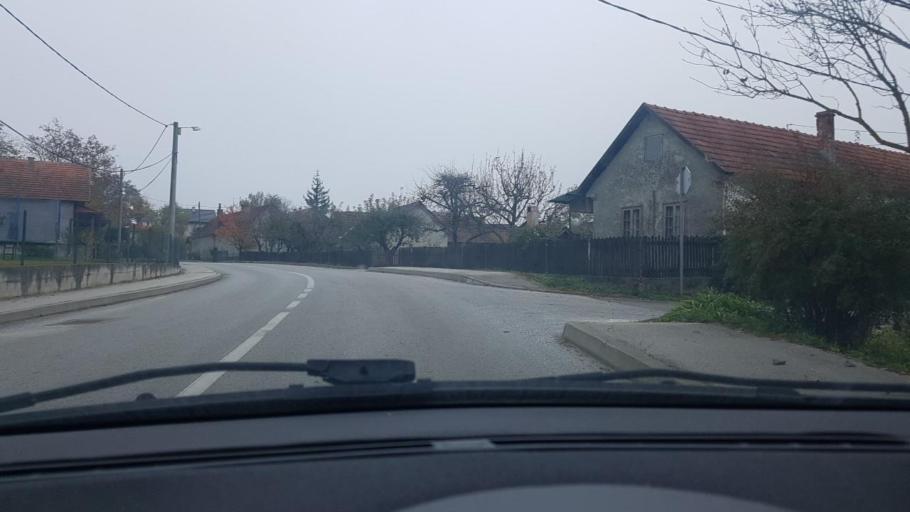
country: HR
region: Varazdinska
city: Ivanec
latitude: 46.1309
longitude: 16.1823
